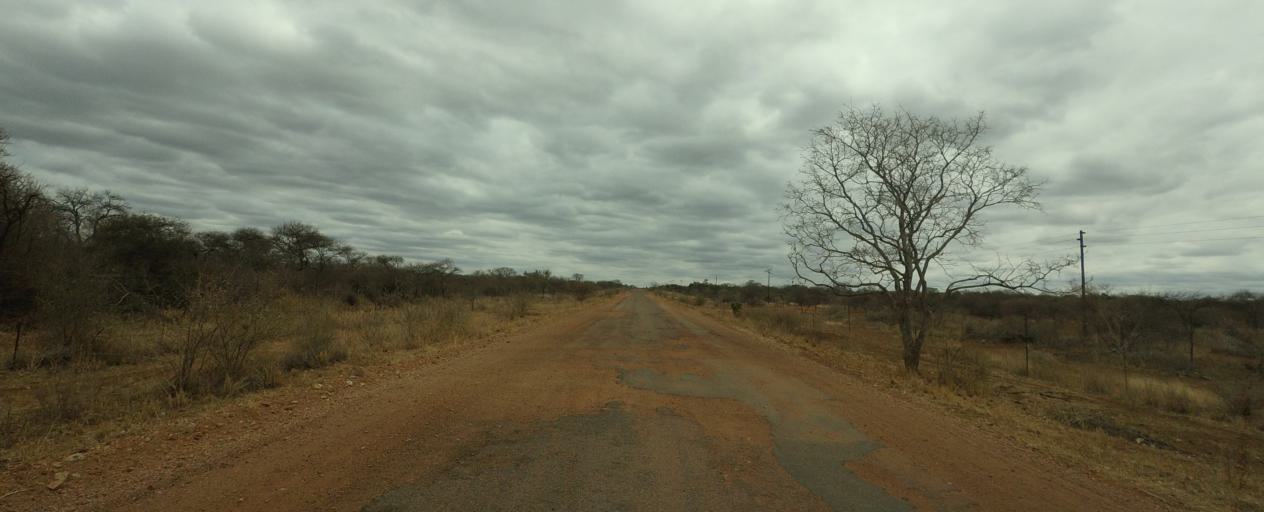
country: BW
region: Central
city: Mathathane
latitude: -22.7393
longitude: 28.4691
